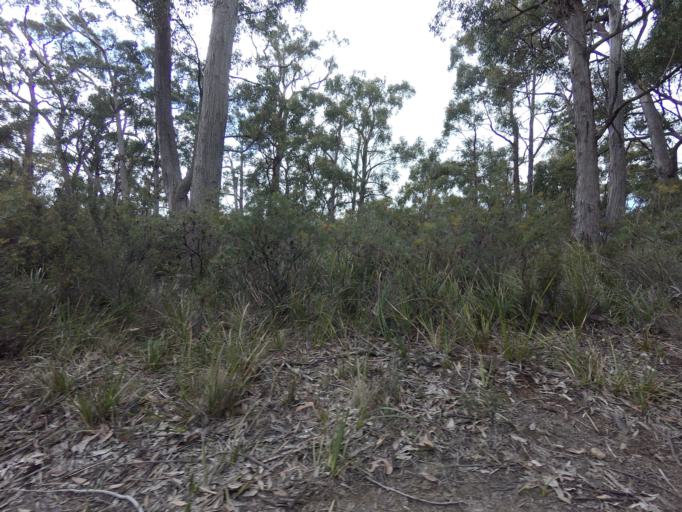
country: AU
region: Tasmania
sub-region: Huon Valley
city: Geeveston
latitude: -43.4763
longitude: 146.9340
